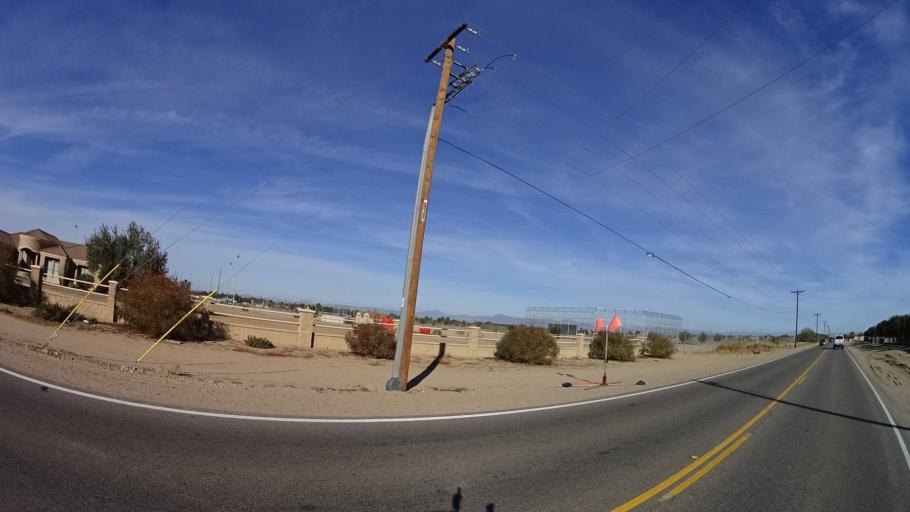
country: US
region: Arizona
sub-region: Maricopa County
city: Queen Creek
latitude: 33.2195
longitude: -111.6803
